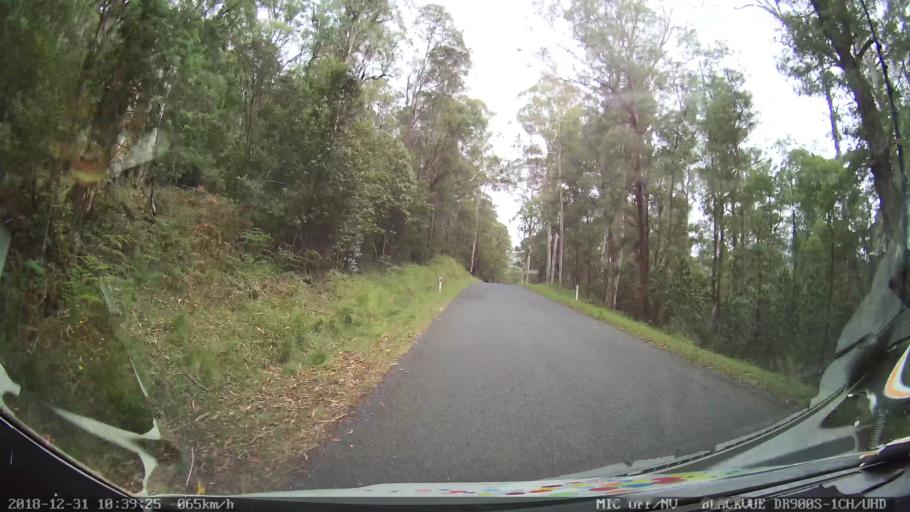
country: AU
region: New South Wales
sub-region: Snowy River
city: Jindabyne
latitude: -36.3993
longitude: 148.1768
